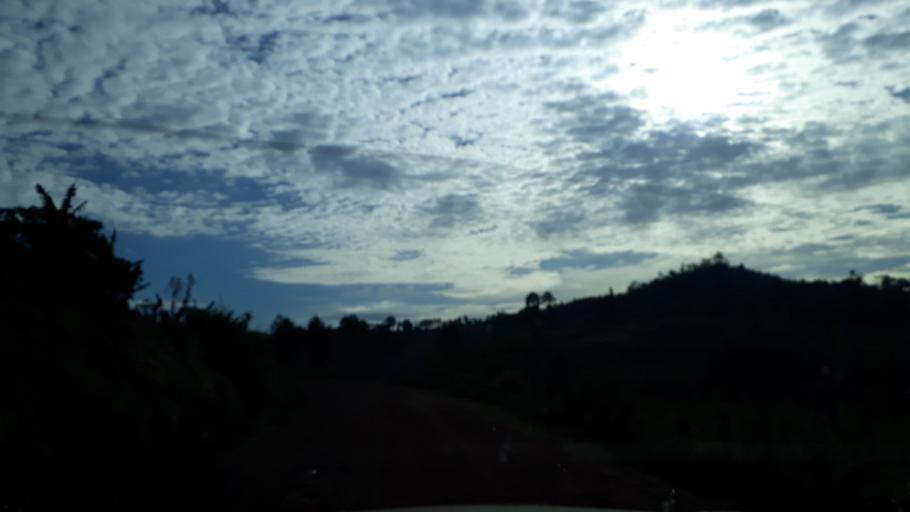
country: UG
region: Northern Region
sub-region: Zombo District
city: Paidha
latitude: 2.2556
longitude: 30.8734
